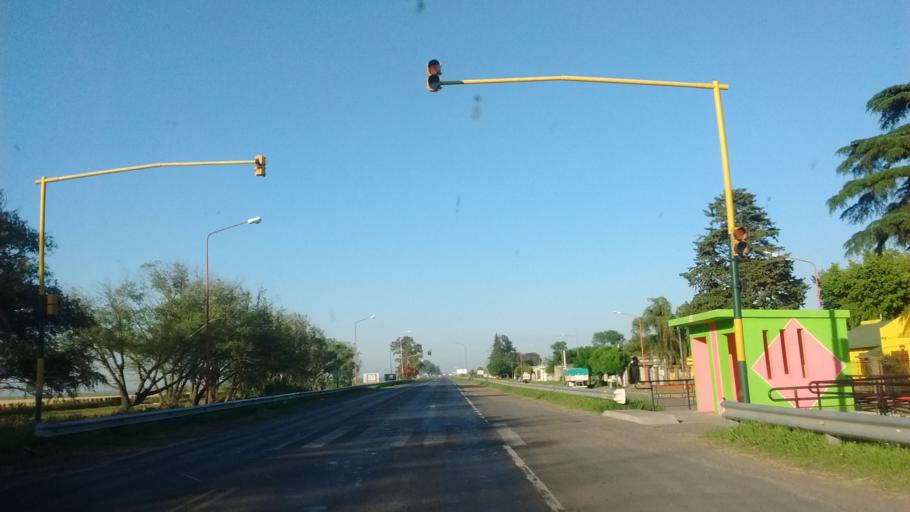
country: AR
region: Santa Fe
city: Venado Tuerto
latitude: -33.6484
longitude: -61.8611
